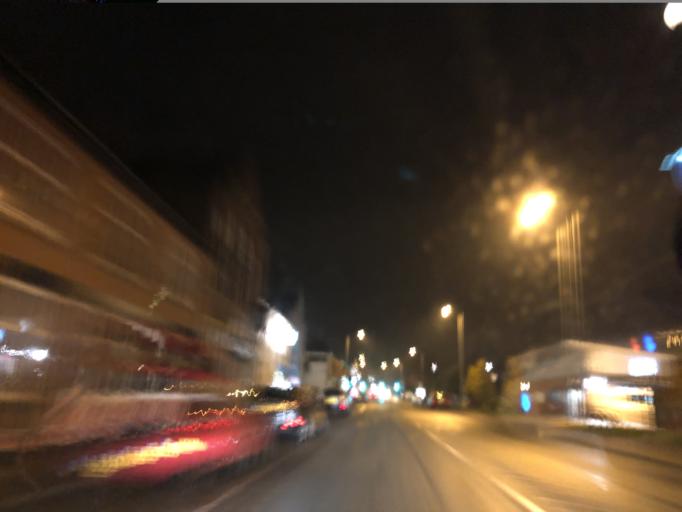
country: GB
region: England
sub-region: Borough of Oldham
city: Shaw
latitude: 53.5615
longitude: -2.0766
